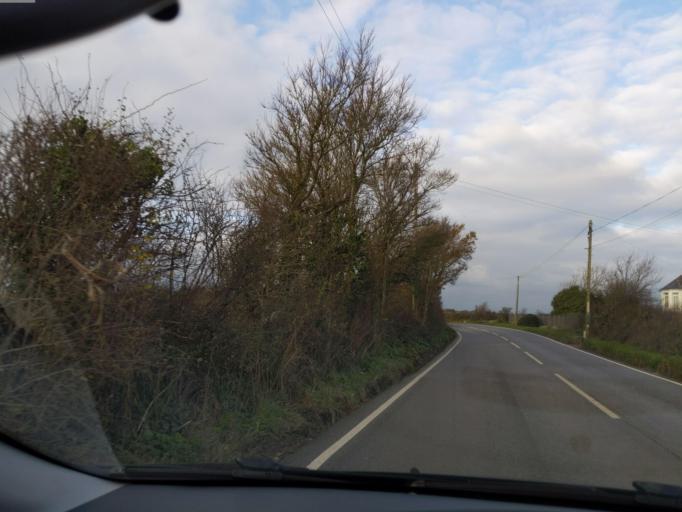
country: GB
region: England
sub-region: Cornwall
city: Padstow
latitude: 50.5166
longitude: -4.9501
